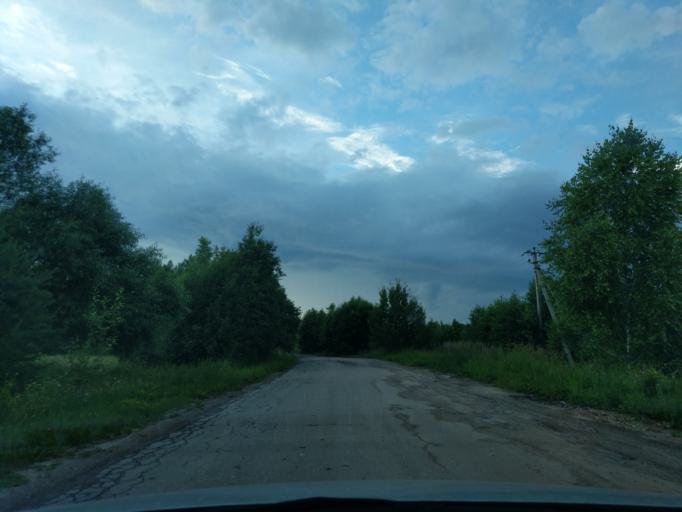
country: RU
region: Kaluga
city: Myatlevo
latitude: 54.8497
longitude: 35.6018
